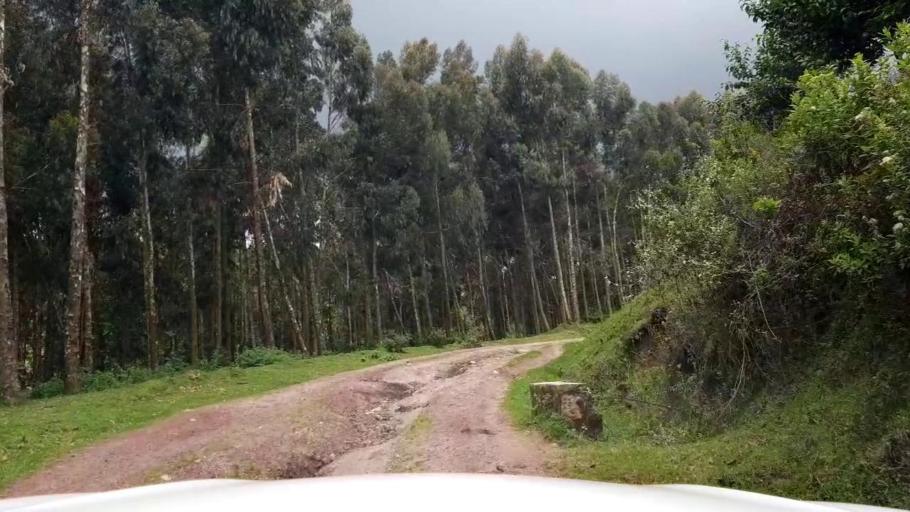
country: RW
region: Western Province
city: Gisenyi
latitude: -1.6881
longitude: 29.4233
